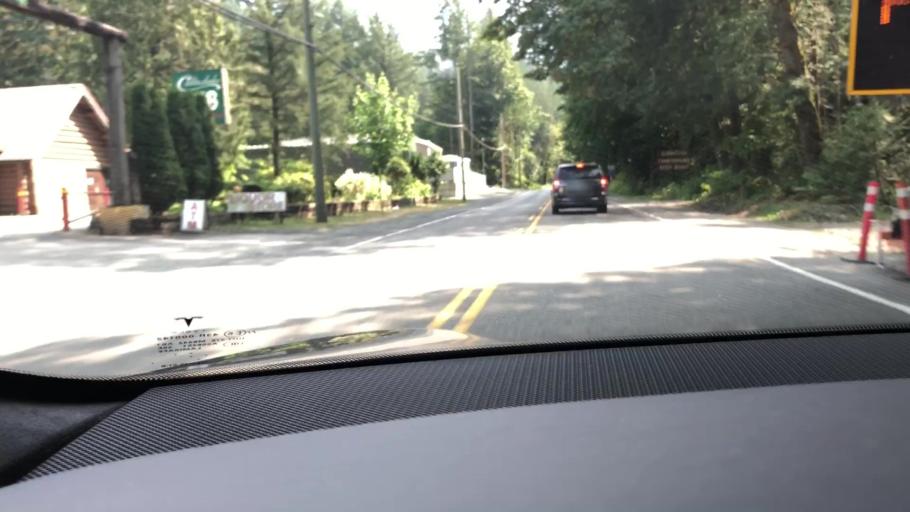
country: CA
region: British Columbia
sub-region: Fraser Valley Regional District
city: Chilliwack
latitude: 49.0702
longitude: -121.9625
